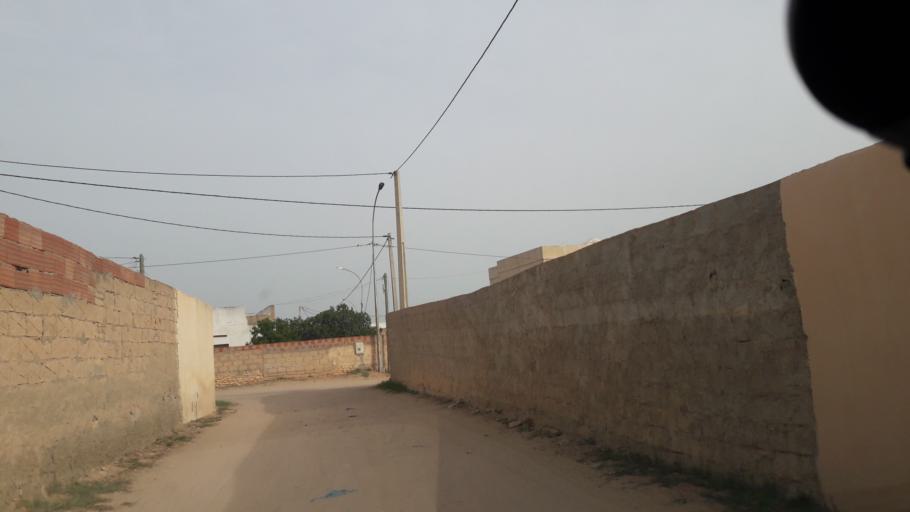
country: TN
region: Safaqis
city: Al Qarmadah
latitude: 34.7786
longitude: 10.7743
